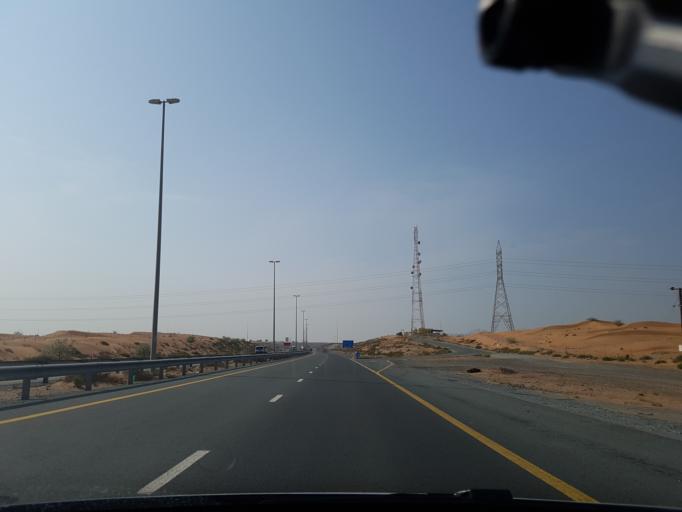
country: AE
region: Umm al Qaywayn
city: Umm al Qaywayn
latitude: 25.5262
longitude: 55.7298
